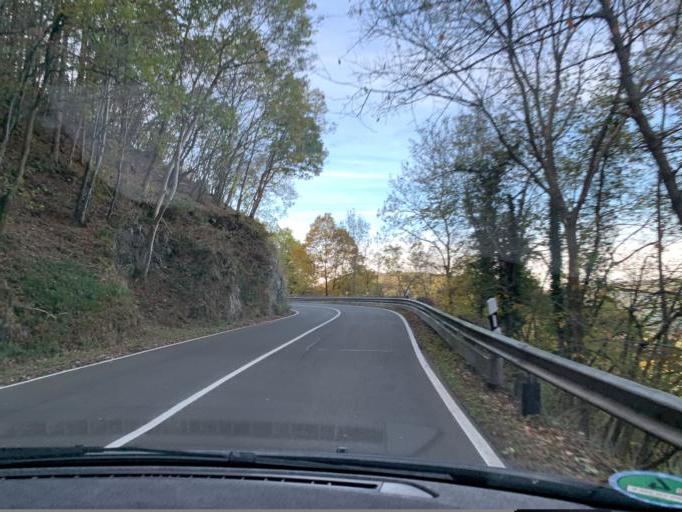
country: DE
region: North Rhine-Westphalia
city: Heimbach
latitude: 50.6274
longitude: 6.4817
